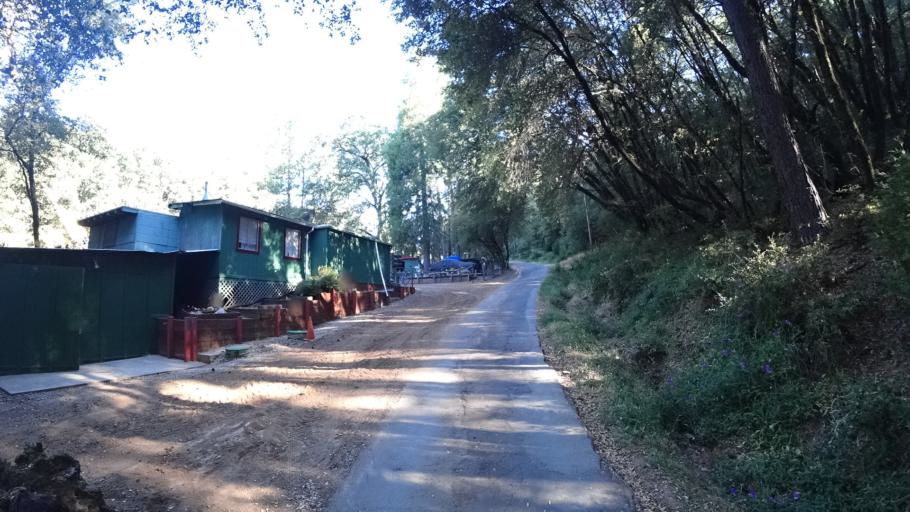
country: US
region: California
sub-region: Amador County
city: Pioneer
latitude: 38.3736
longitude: -120.5535
